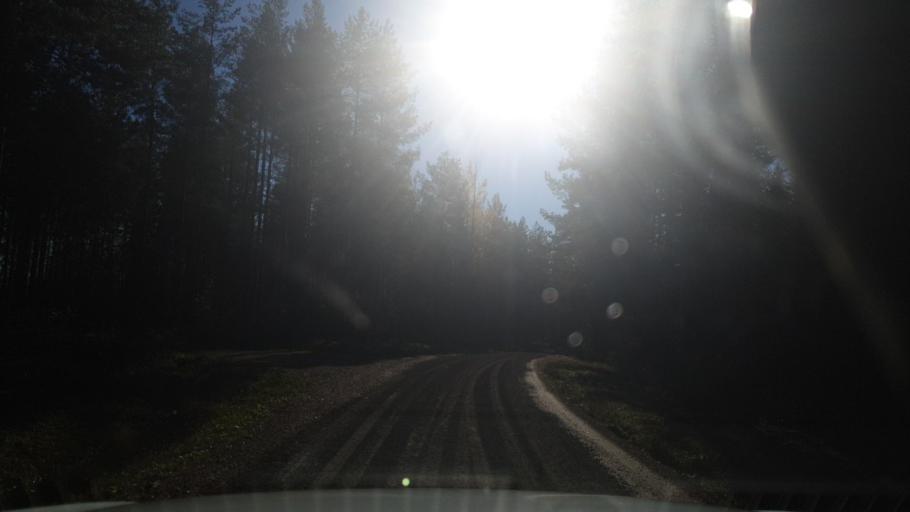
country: SE
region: Vaermland
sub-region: Grums Kommun
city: Grums
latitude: 59.4706
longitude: 12.9243
